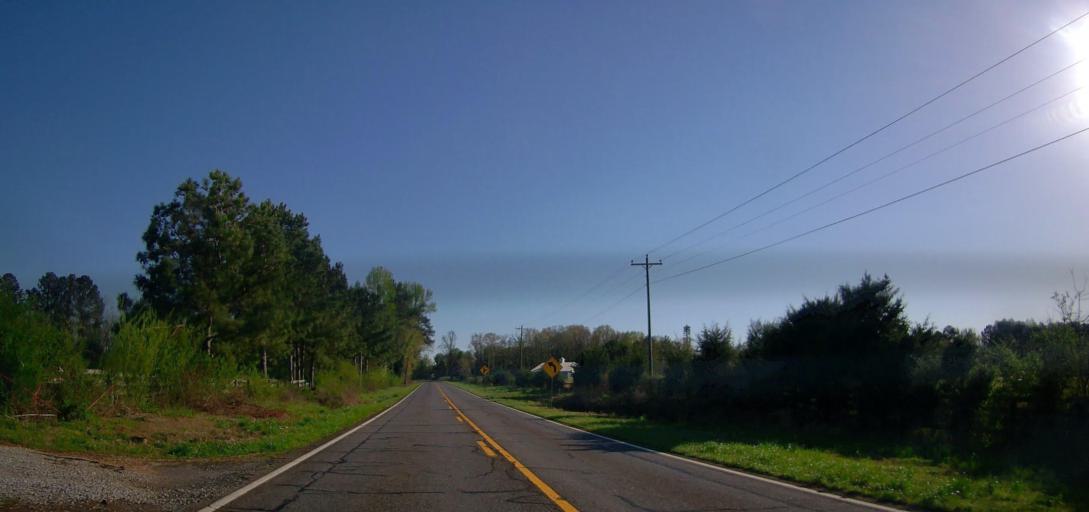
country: US
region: Georgia
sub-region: Butts County
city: Indian Springs
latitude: 33.1832
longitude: -83.9586
